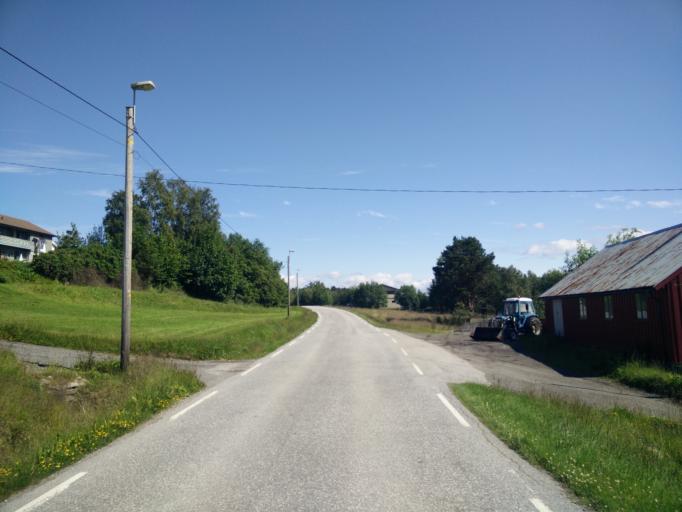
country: NO
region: More og Romsdal
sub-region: Kristiansund
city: Rensvik
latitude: 63.0462
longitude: 7.8555
